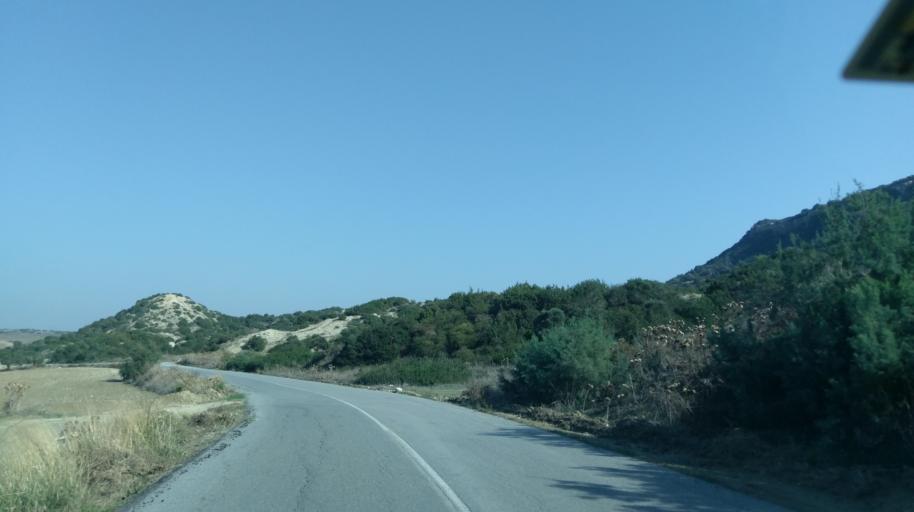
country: CY
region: Ammochostos
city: Leonarisso
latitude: 35.5005
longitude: 34.2331
